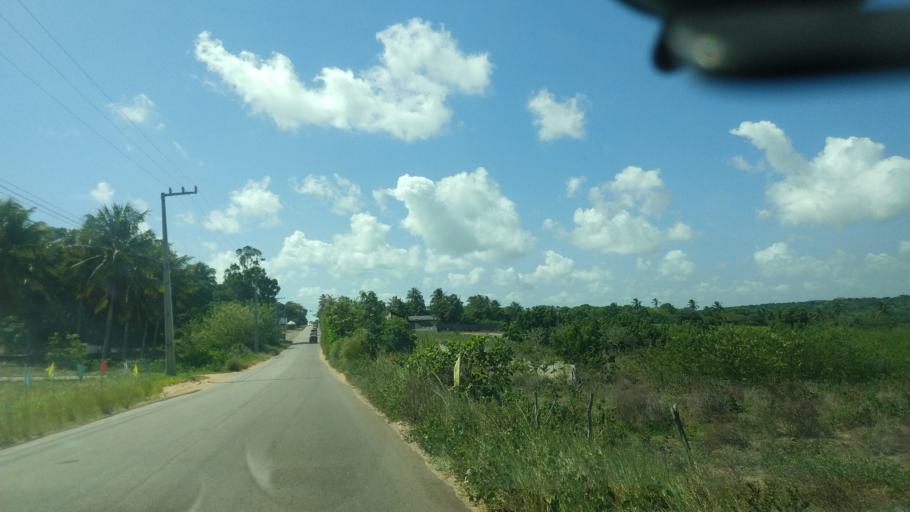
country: BR
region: Rio Grande do Norte
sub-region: Parnamirim
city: Parnamirim
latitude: -5.9482
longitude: -35.1815
